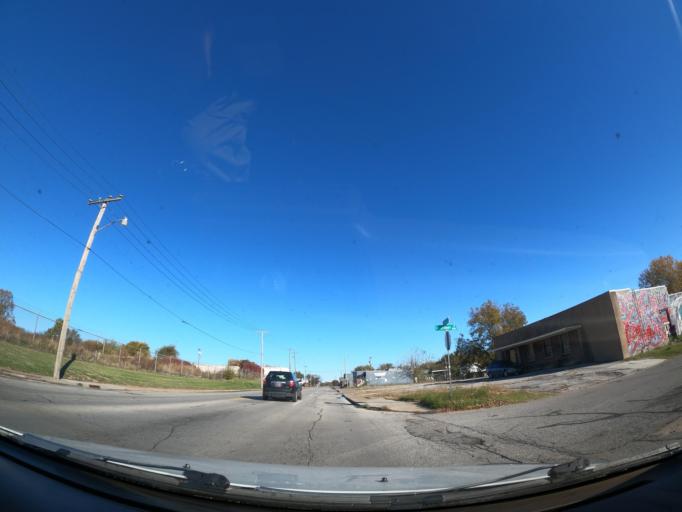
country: US
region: Oklahoma
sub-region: Tulsa County
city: Tulsa
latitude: 36.1712
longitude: -95.9671
